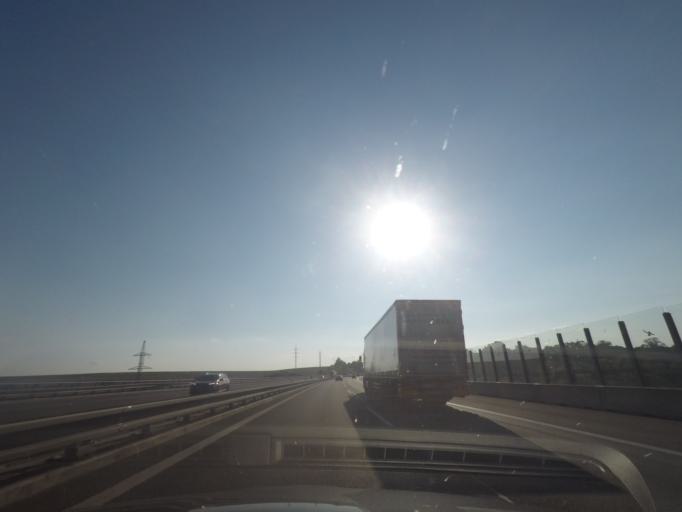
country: CZ
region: Olomoucky
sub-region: Okres Olomouc
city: Olomouc
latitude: 49.5488
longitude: 17.2495
